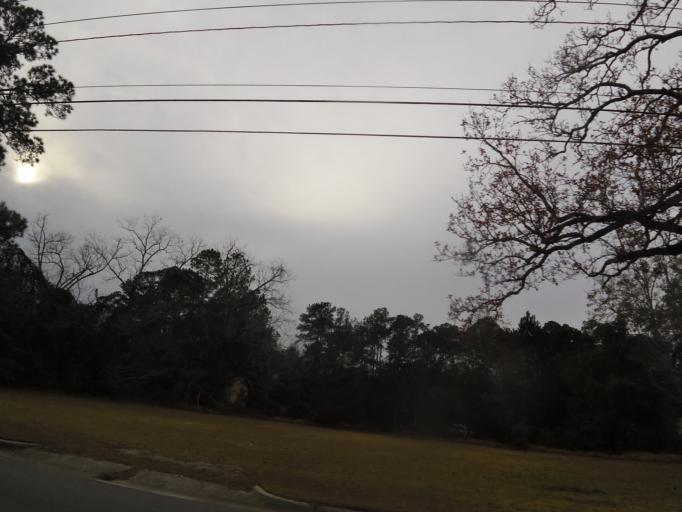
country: US
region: Georgia
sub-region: Thomas County
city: Thomasville
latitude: 30.8176
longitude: -83.9796
